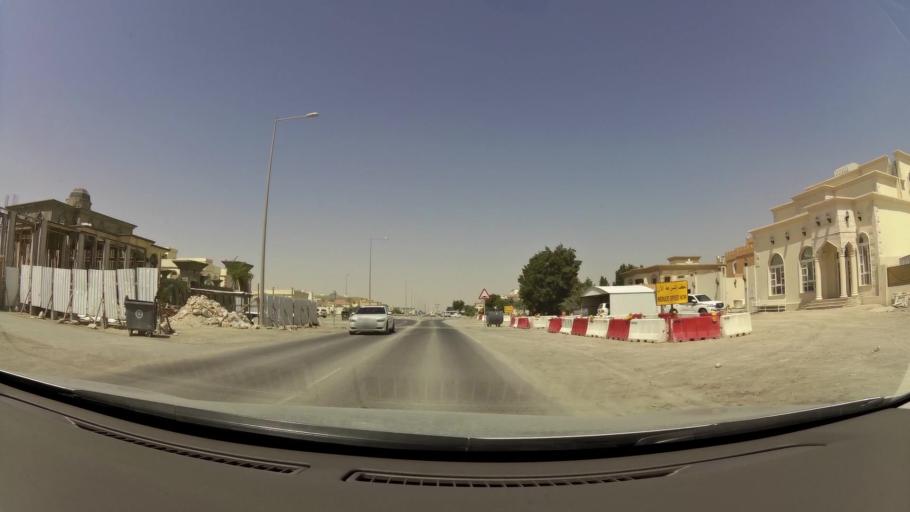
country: QA
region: Baladiyat ar Rayyan
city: Ar Rayyan
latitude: 25.2500
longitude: 51.4024
